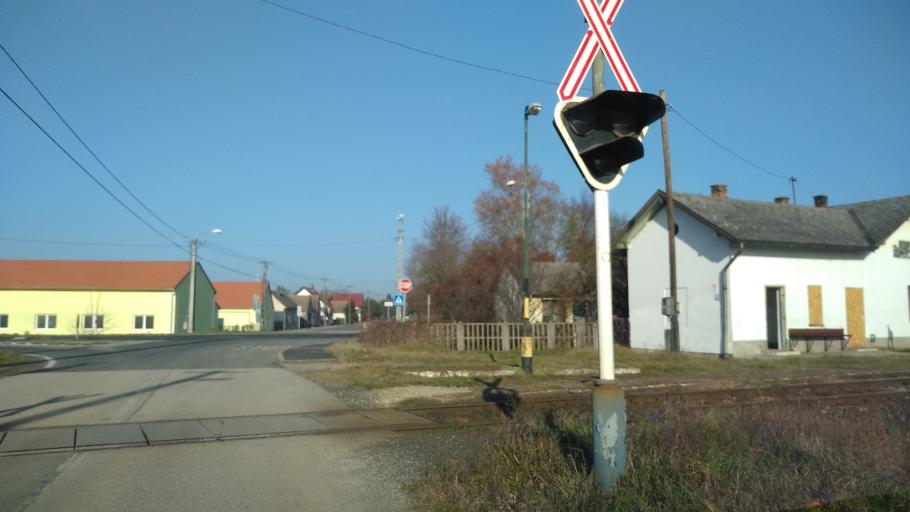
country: HU
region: Somogy
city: Barcs
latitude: 45.9581
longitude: 17.4859
